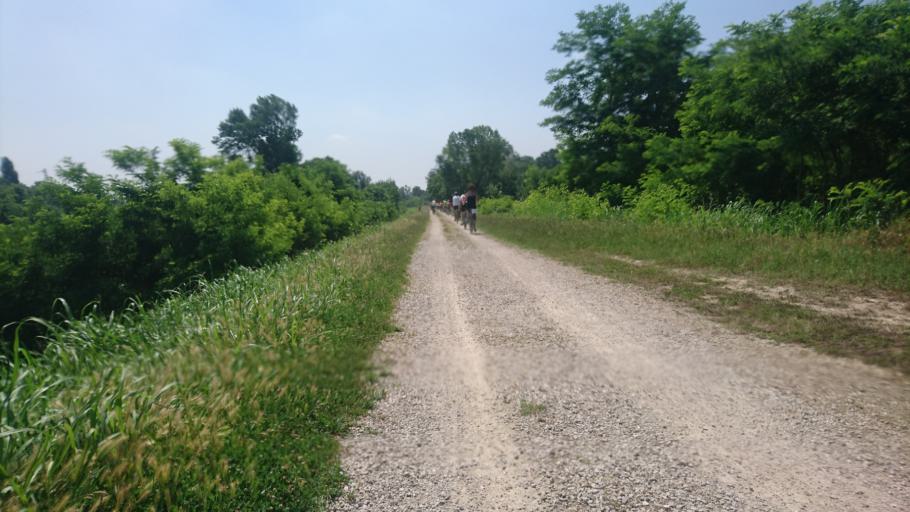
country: IT
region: Veneto
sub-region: Provincia di Venezia
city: Vigonovo
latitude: 45.3949
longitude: 12.0080
